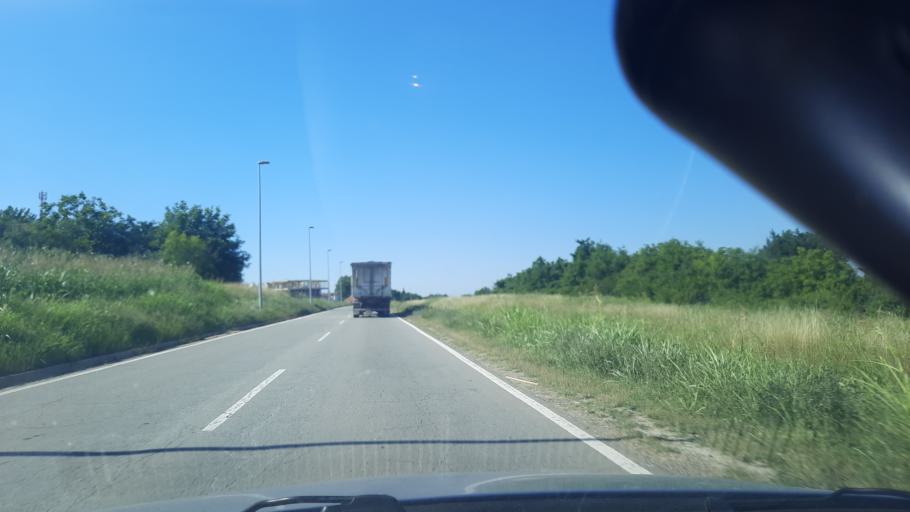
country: RS
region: Autonomna Pokrajina Vojvodina
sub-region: Juznobacki Okrug
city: Novi Sad
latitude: 45.2152
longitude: 19.8377
